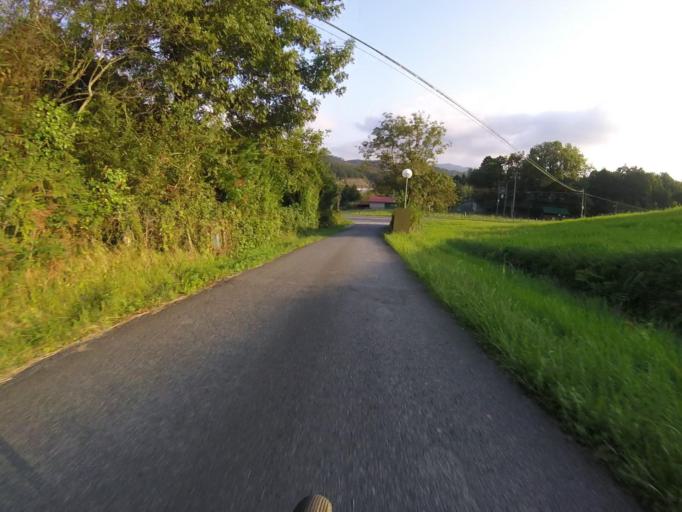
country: ES
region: Basque Country
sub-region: Provincia de Guipuzcoa
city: Lezo
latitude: 43.3288
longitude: -1.8622
